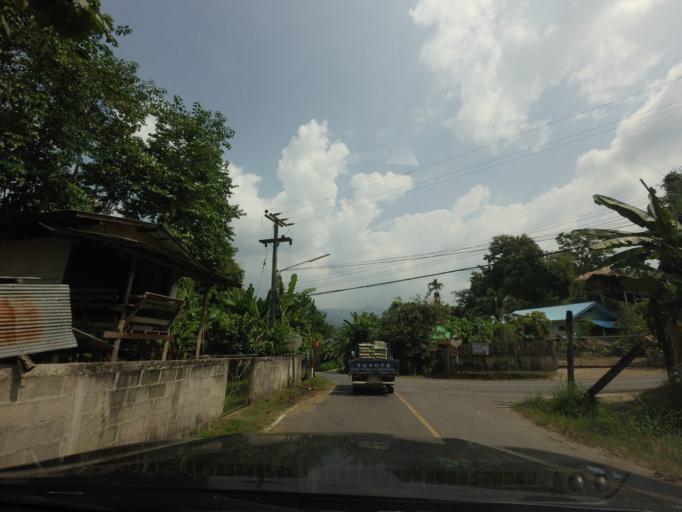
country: TH
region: Nan
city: Pua
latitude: 19.1667
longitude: 100.9325
